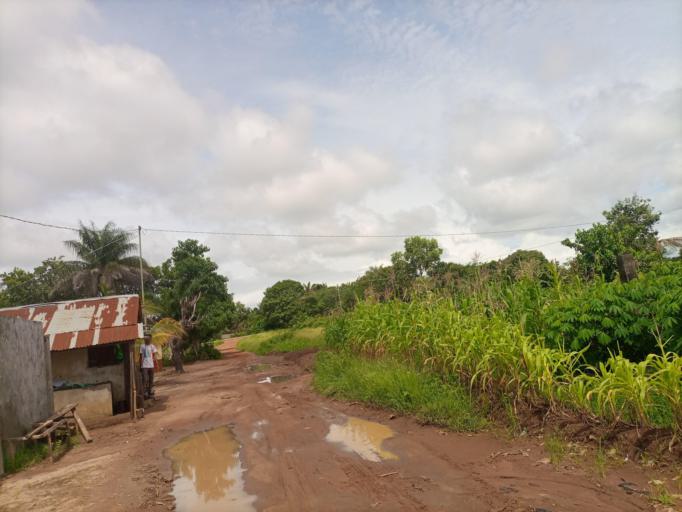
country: SL
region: Northern Province
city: Masoyila
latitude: 8.6133
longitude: -13.1749
